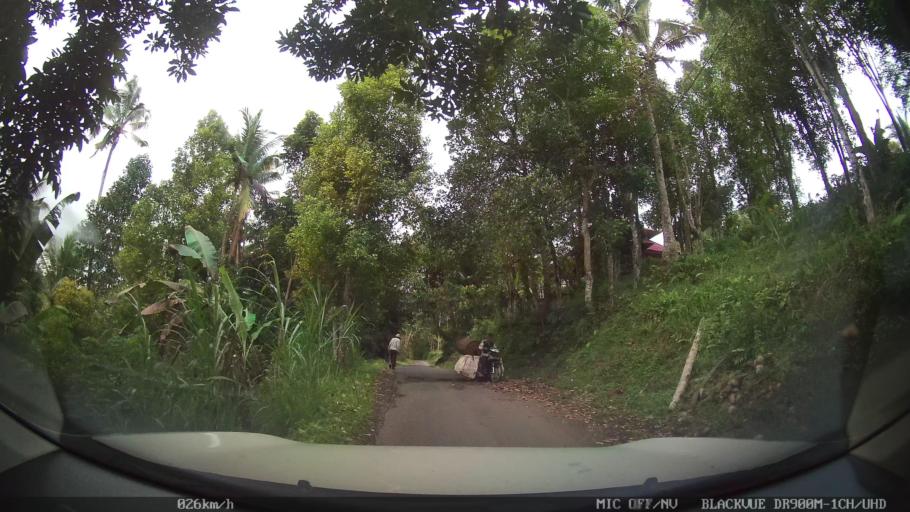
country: ID
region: Bali
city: Banjar Wangsian
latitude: -8.4598
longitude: 115.4162
